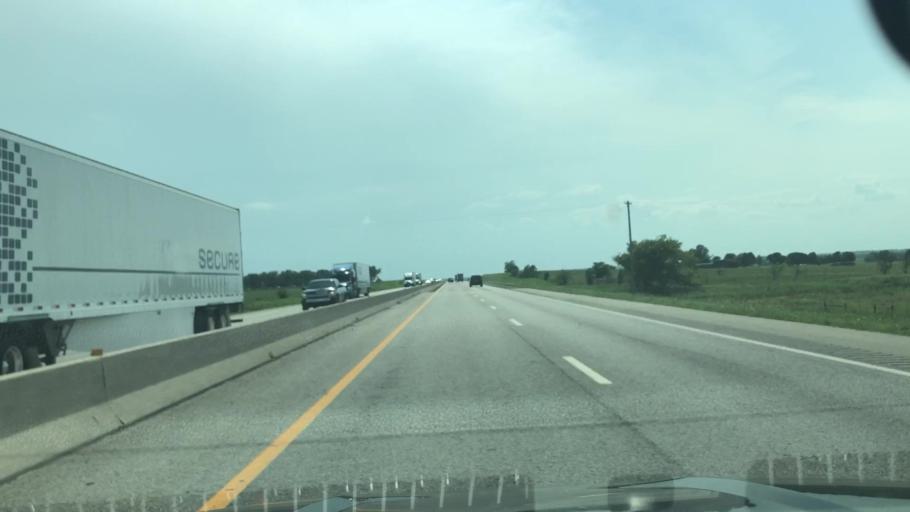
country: US
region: Oklahoma
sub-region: Ottawa County
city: Afton
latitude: 36.6990
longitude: -94.9981
